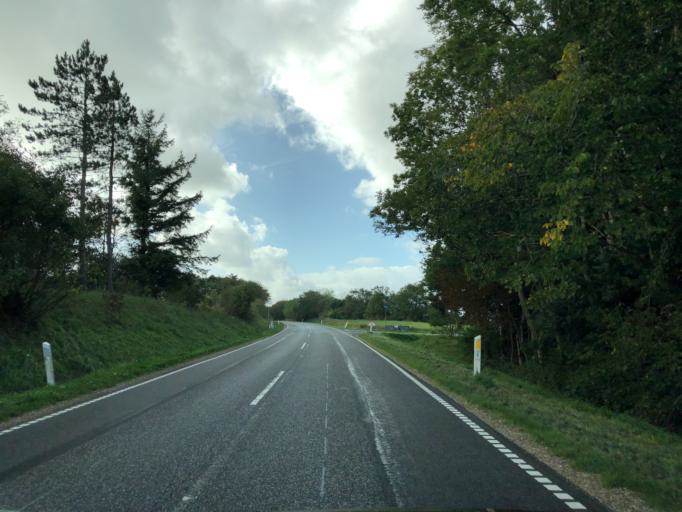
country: DK
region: Central Jutland
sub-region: Holstebro Kommune
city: Holstebro
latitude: 56.3726
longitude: 8.5183
